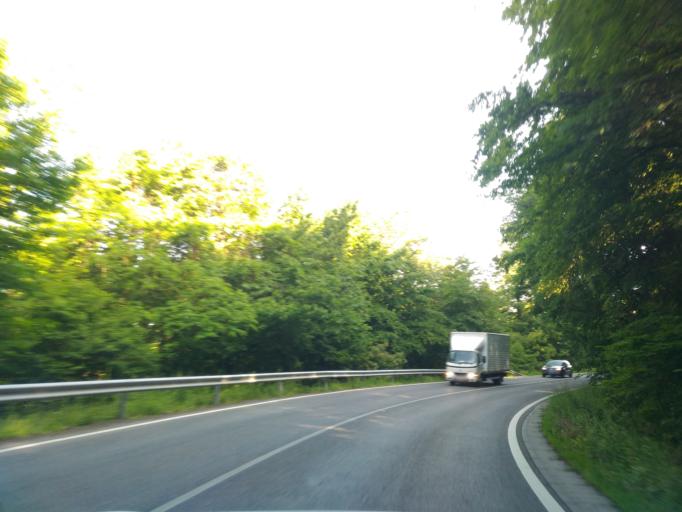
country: HU
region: Baranya
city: Komlo
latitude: 46.1797
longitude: 18.2623
